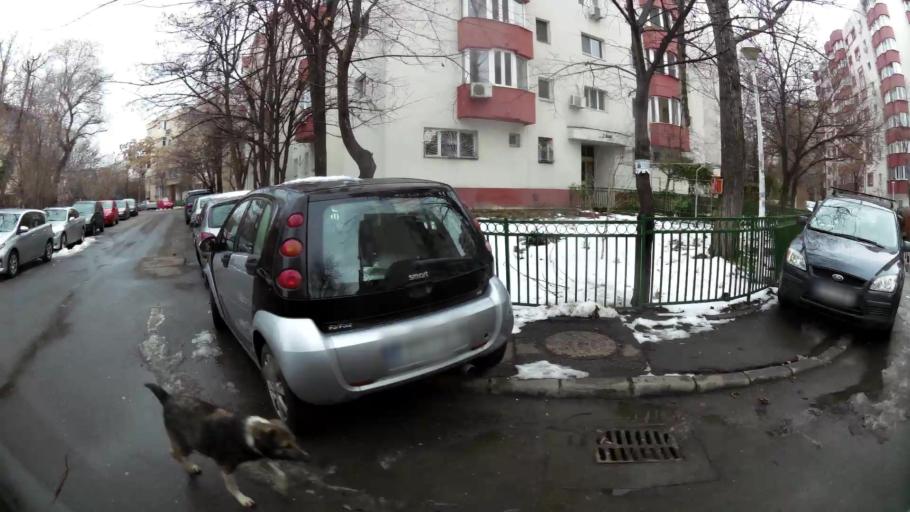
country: RO
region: Bucuresti
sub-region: Municipiul Bucuresti
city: Bucuresti
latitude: 44.4220
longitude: 26.0620
